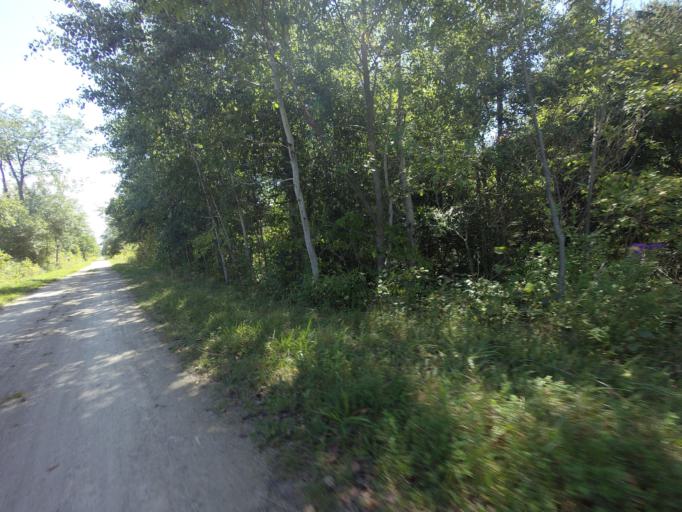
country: CA
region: Ontario
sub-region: Wellington County
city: Guelph
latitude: 43.7376
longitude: -80.3491
